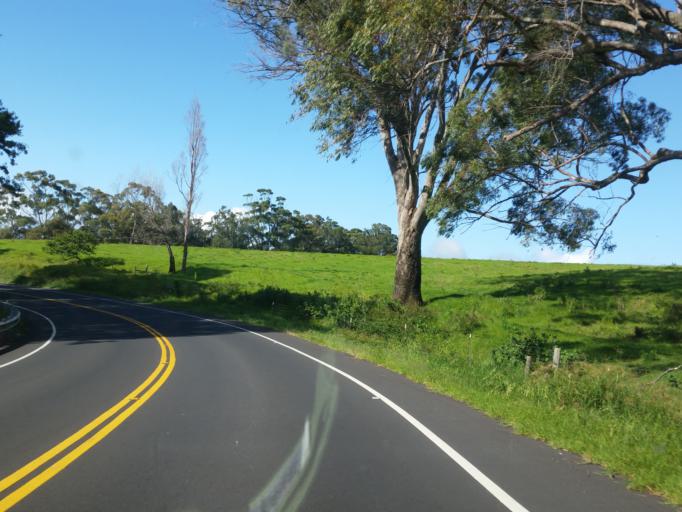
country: US
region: Hawaii
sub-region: Maui County
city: Pukalani
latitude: 20.8256
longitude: -156.3152
